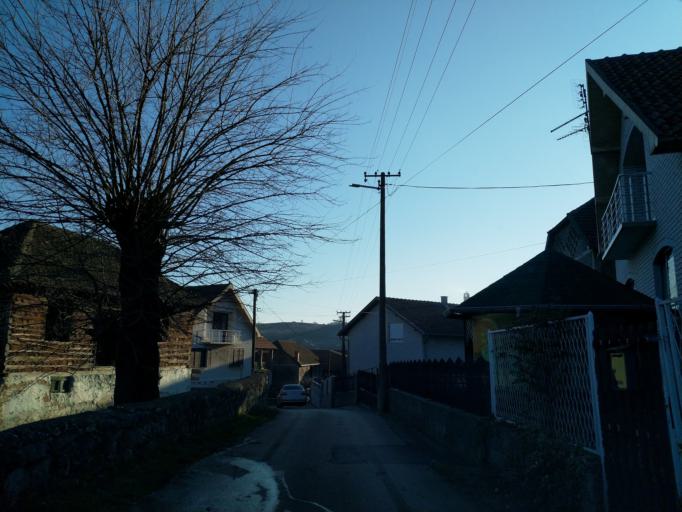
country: RS
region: Central Serbia
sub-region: Pomoravski Okrug
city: Paracin
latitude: 43.9367
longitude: 21.5221
